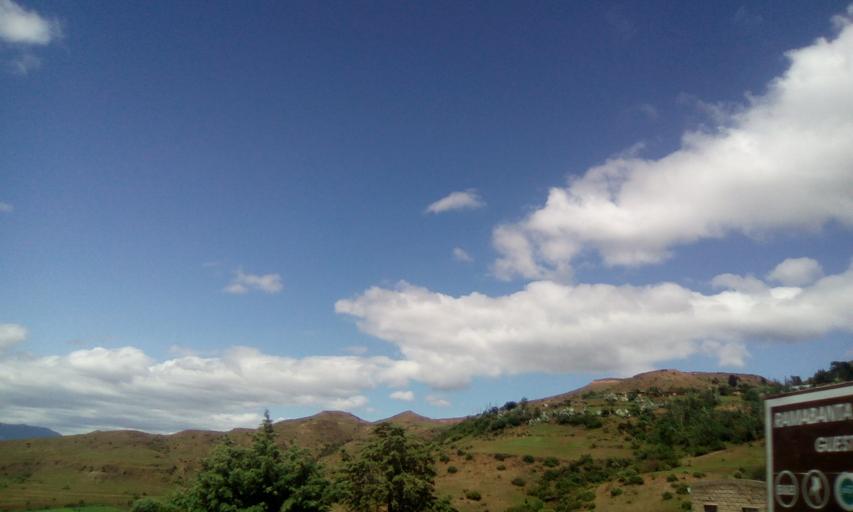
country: LS
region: Maseru
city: Nako
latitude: -29.6643
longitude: 27.7935
